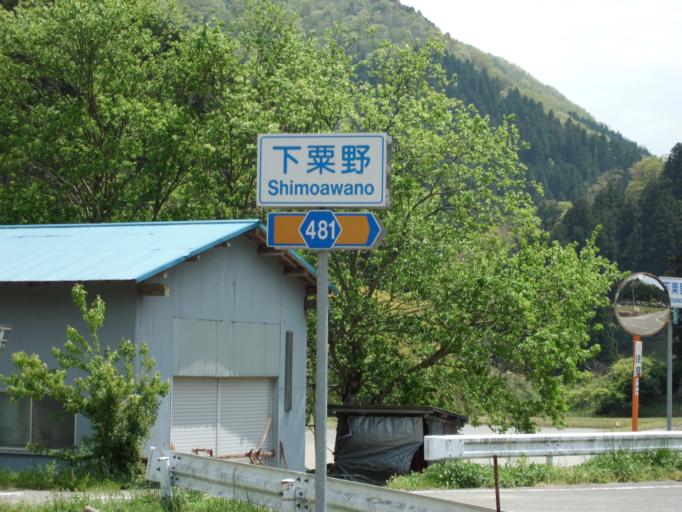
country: JP
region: Kyoto
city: Ayabe
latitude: 35.2992
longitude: 135.4257
